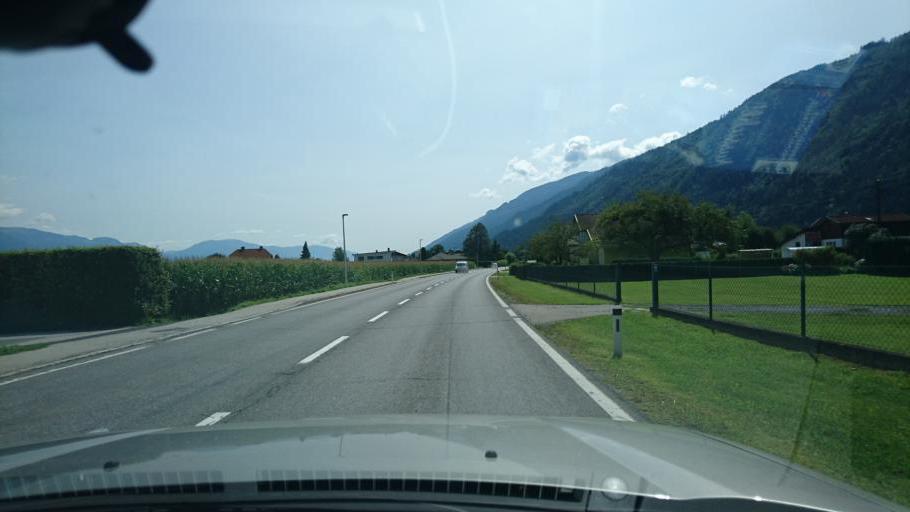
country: AT
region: Carinthia
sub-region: Politischer Bezirk Spittal an der Drau
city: Sachsenburg
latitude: 46.8362
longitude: 13.3753
